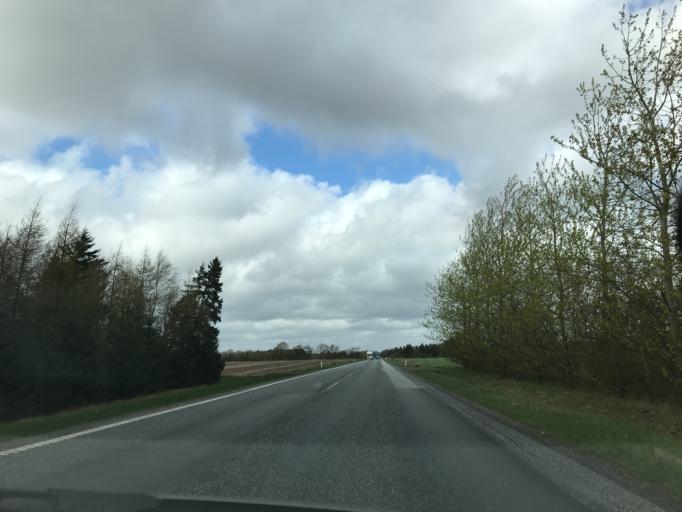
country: DK
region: Central Jutland
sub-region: Viborg Kommune
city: Stoholm
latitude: 56.3951
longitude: 8.9984
